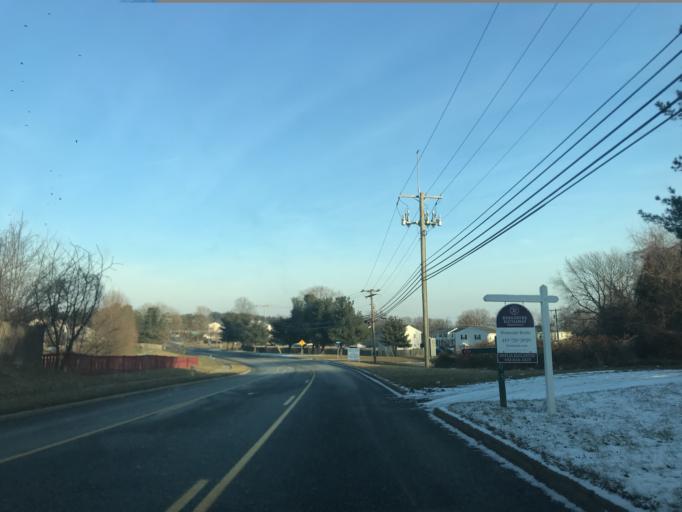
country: US
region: Maryland
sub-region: Harford County
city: Edgewood
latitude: 39.4227
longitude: -76.3251
